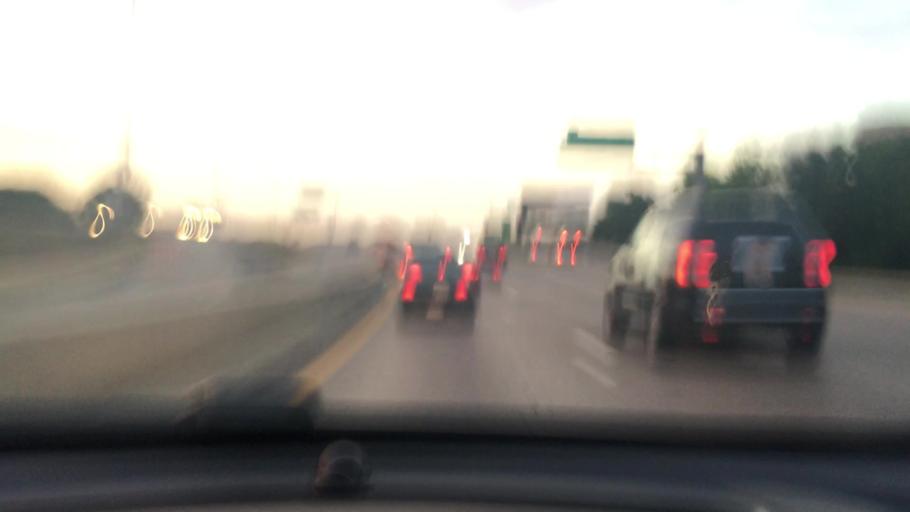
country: US
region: Texas
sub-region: Dallas County
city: Cockrell Hill
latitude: 32.7076
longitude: -96.8295
